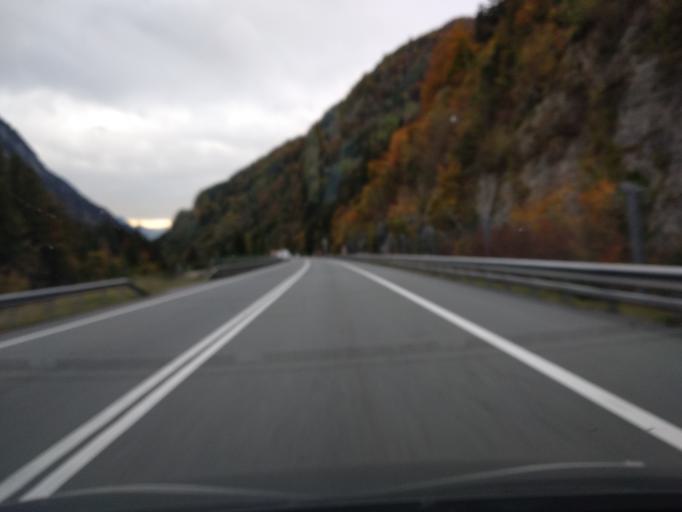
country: AT
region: Vorarlberg
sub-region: Politischer Bezirk Bludenz
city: Dalaas
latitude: 47.1271
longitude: 9.9802
